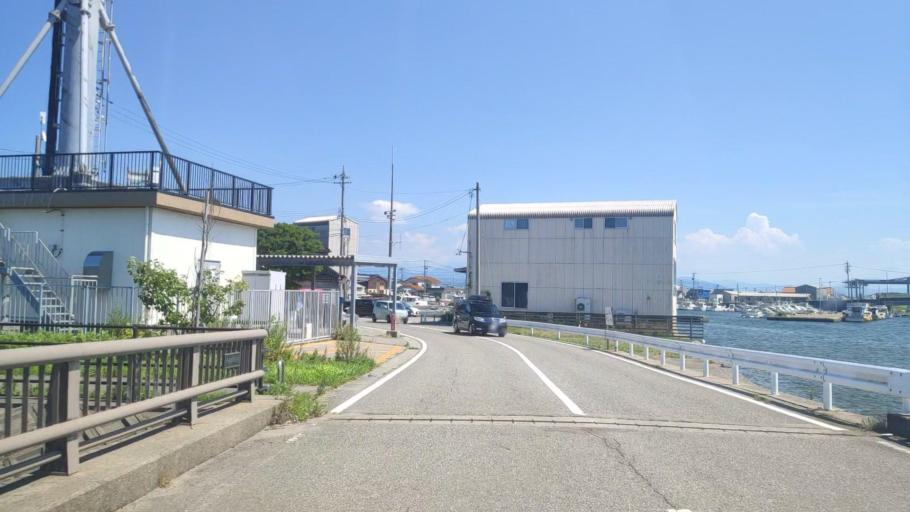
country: JP
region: Ishikawa
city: Kanazawa-shi
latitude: 36.5990
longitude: 136.5899
